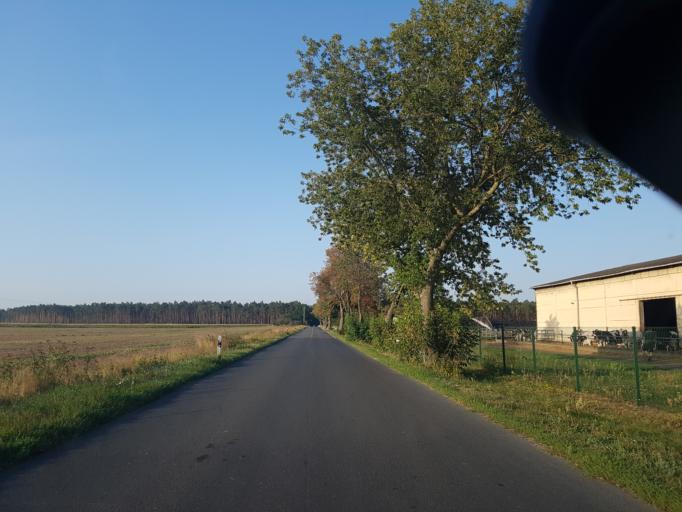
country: DE
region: Saxony-Anhalt
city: Holzdorf
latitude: 51.8106
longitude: 13.1432
